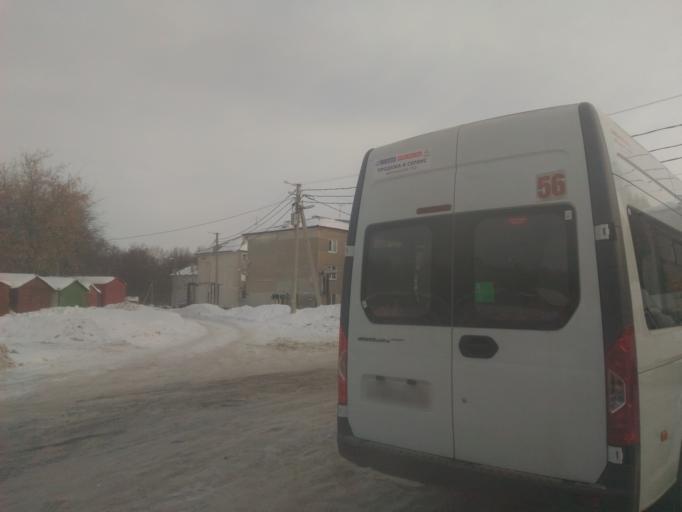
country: RU
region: Ulyanovsk
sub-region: Ulyanovskiy Rayon
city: Ulyanovsk
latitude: 54.3667
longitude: 48.3511
